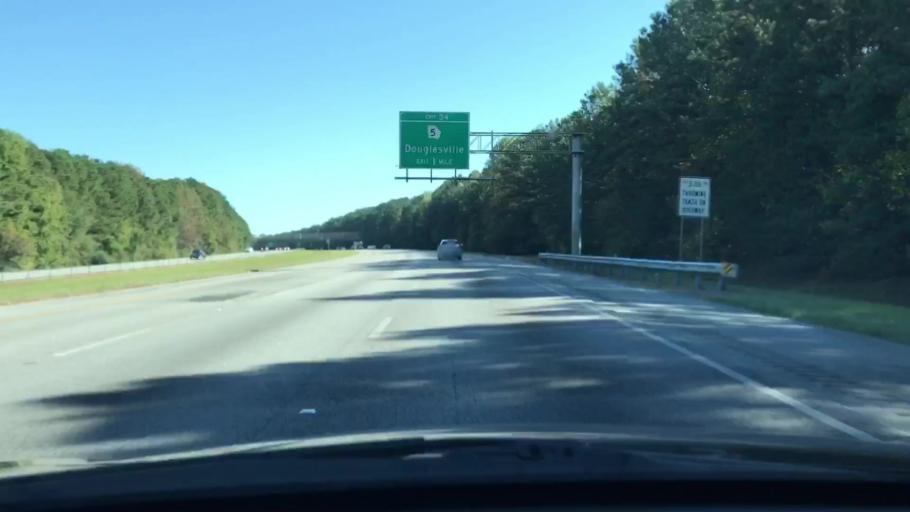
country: US
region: Georgia
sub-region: Douglas County
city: Douglasville
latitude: 33.7221
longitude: -84.7821
